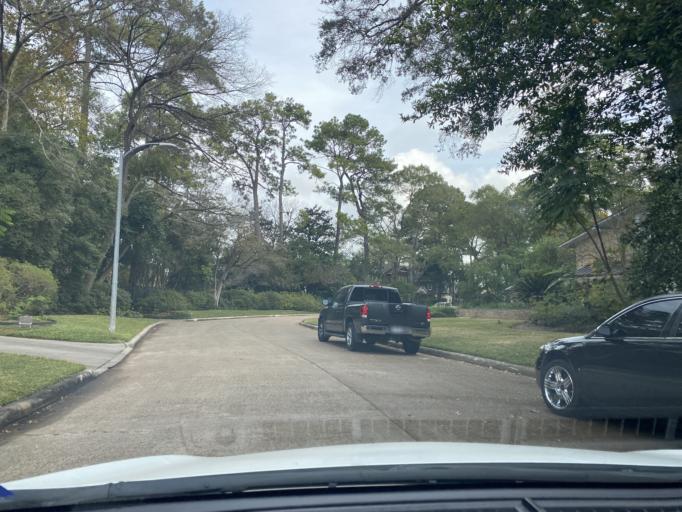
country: US
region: Texas
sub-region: Harris County
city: Hunters Creek Village
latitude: 29.7660
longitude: -95.4655
